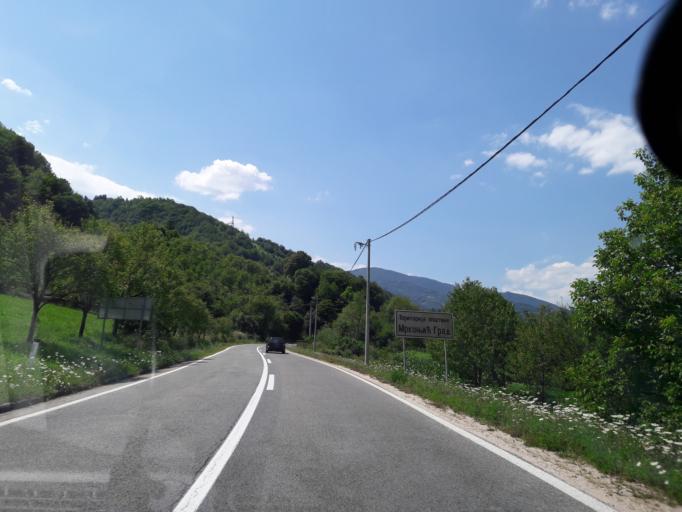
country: BA
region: Republika Srpska
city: Mrkonjic Grad
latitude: 44.3678
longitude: 17.1485
